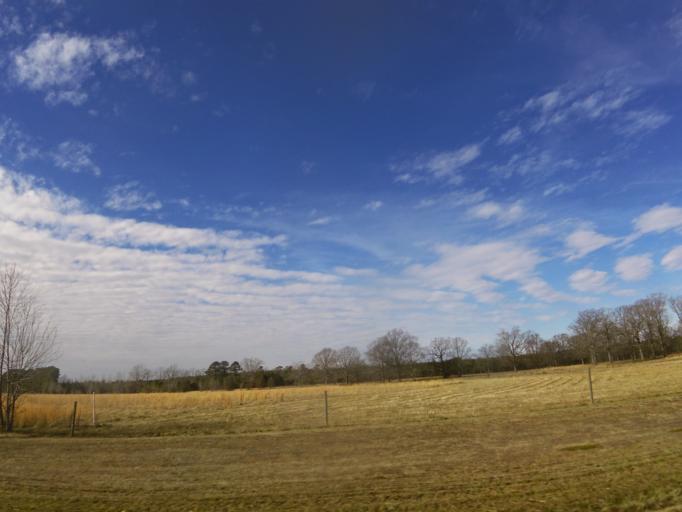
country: US
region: Virginia
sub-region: City of Franklin
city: Franklin
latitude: 36.7020
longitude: -76.8894
